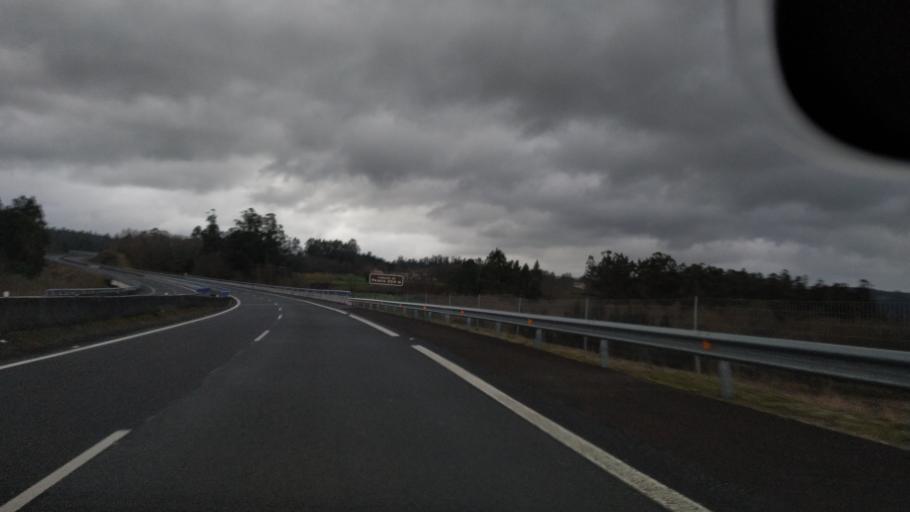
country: ES
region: Galicia
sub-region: Provincia da Coruna
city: Vedra
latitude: 42.8109
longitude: -8.4817
